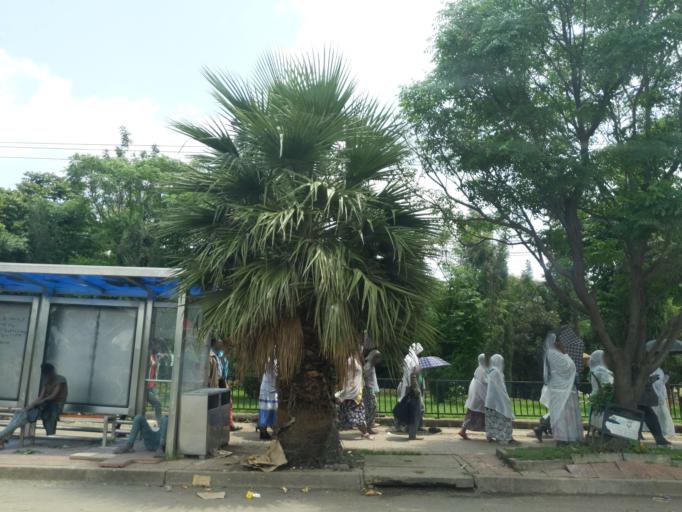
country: ET
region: Adis Abeba
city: Addis Ababa
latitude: 8.9504
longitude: 38.7637
